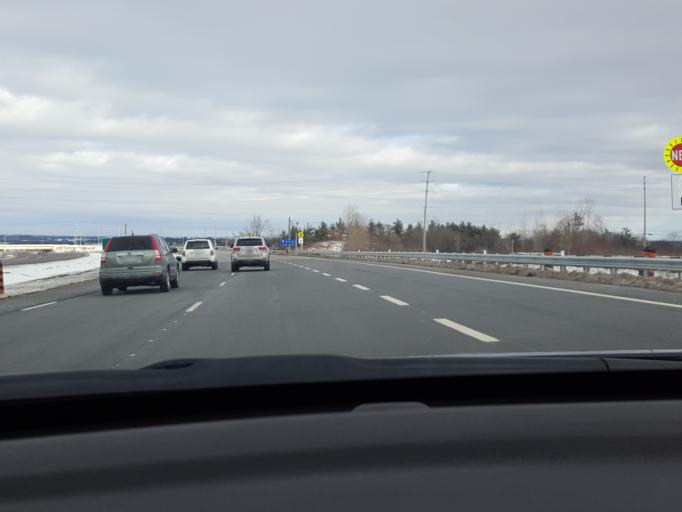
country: CA
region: Ontario
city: Pickering
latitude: 43.9136
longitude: -79.1065
